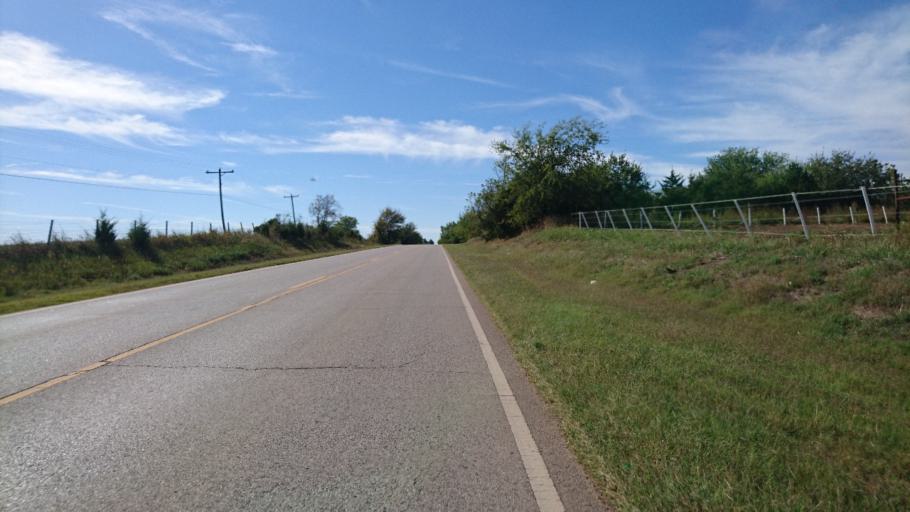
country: US
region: Oklahoma
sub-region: Lincoln County
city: Chandler
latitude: 35.7099
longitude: -96.7991
